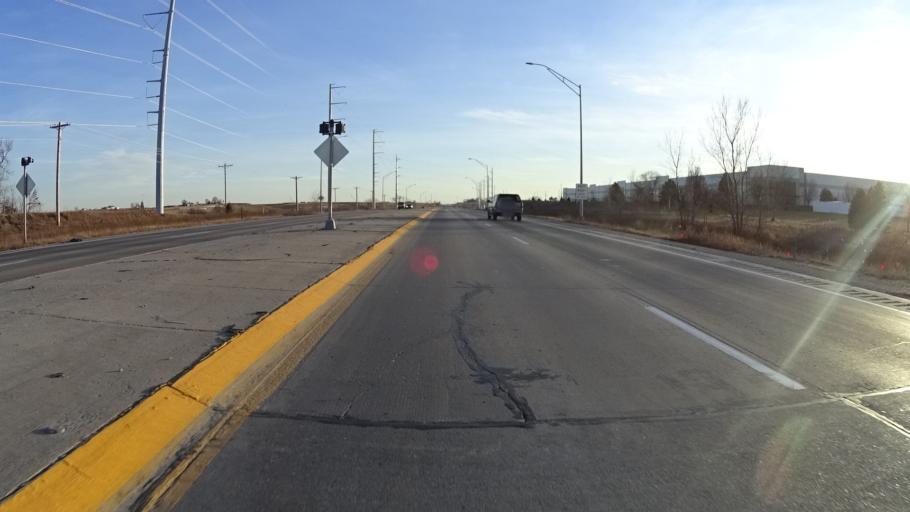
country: US
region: Nebraska
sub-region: Sarpy County
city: Chalco
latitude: 41.1450
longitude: -96.1390
